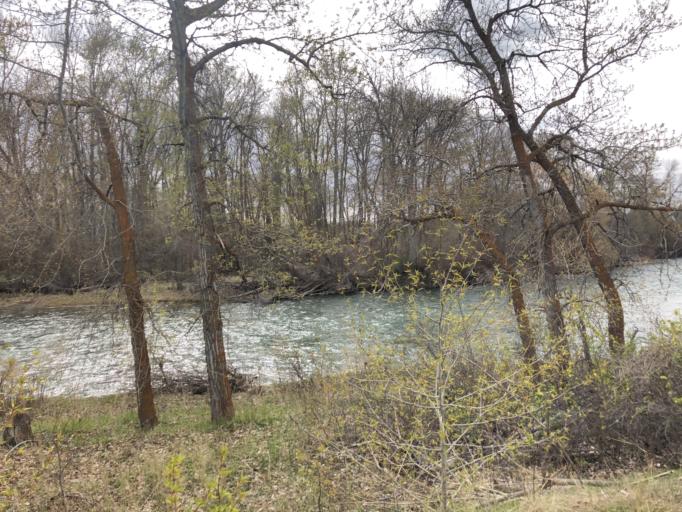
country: US
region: Washington
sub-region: Kittitas County
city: Ellensburg
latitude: 46.9910
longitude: -120.5766
